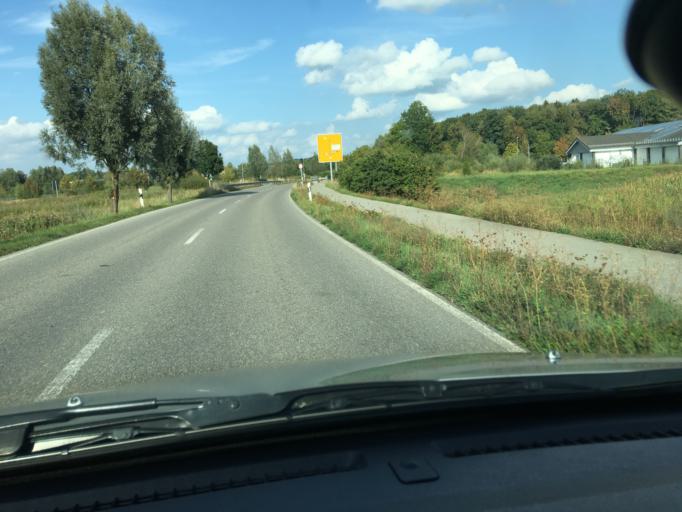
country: DE
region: Baden-Wuerttemberg
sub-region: Tuebingen Region
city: Bad Schussenried
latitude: 47.9967
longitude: 9.6609
